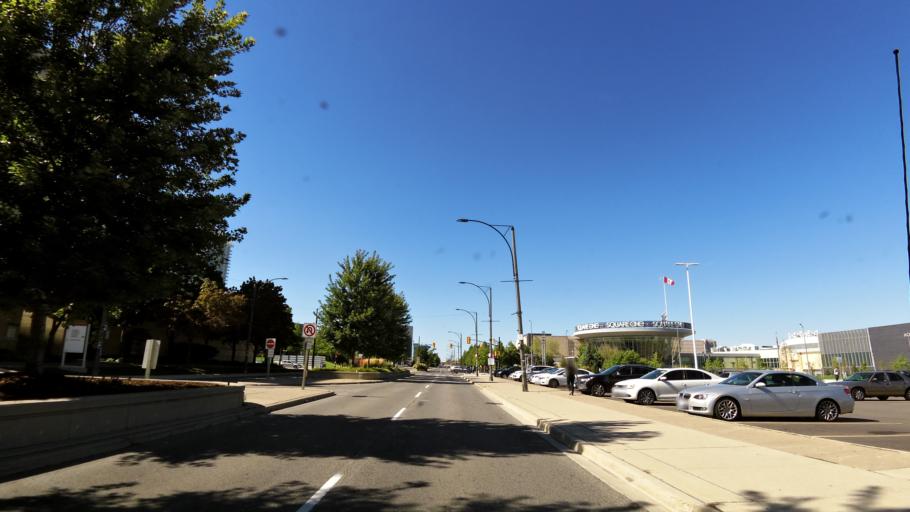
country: CA
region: Ontario
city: Mississauga
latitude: 43.5893
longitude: -79.6433
